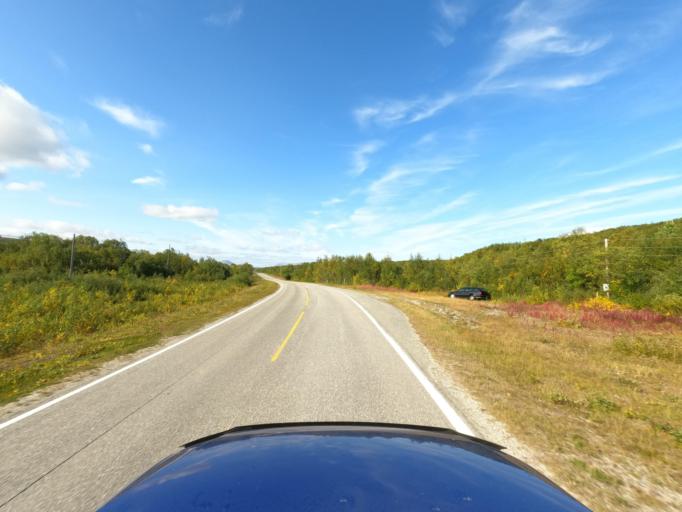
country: NO
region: Finnmark Fylke
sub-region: Porsanger
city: Lakselv
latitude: 69.7629
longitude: 25.1986
